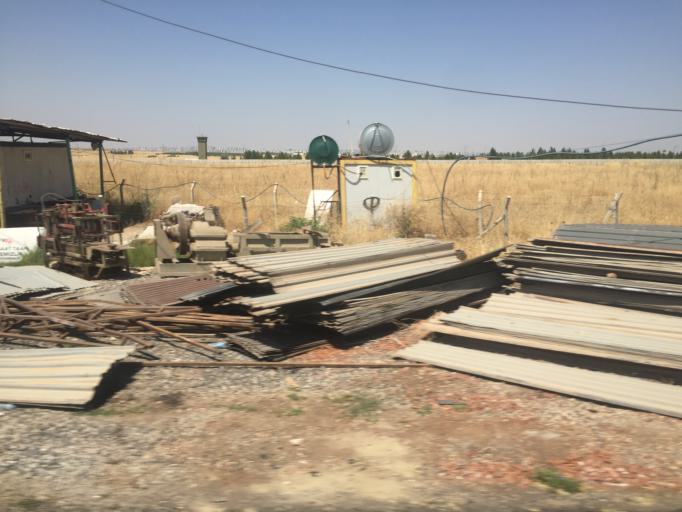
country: TR
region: Diyarbakir
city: Diyarbakir
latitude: 37.8712
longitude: 40.2165
